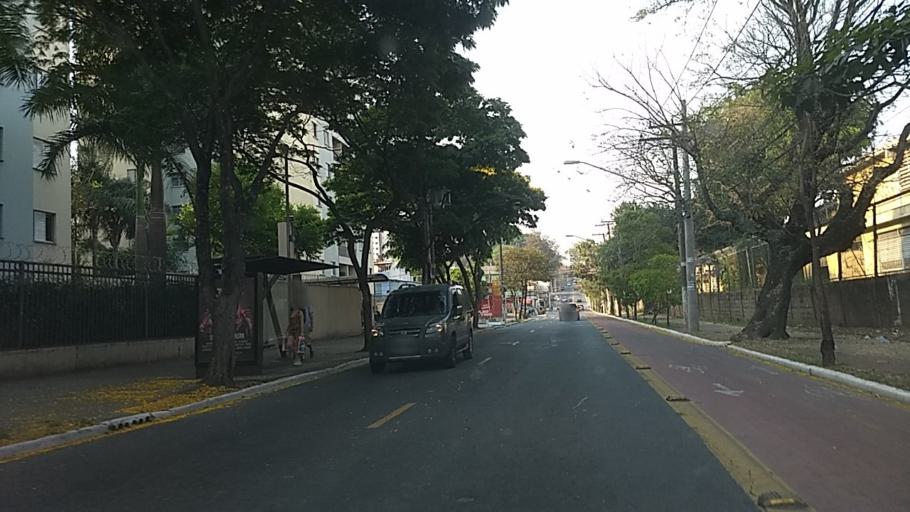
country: BR
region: Sao Paulo
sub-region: Sao Paulo
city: Sao Paulo
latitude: -23.5105
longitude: -46.6012
